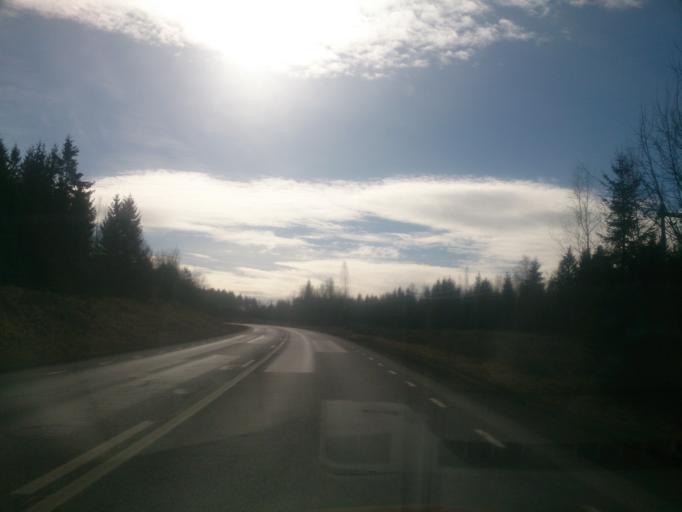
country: SE
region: OEstergoetland
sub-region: Norrkopings Kommun
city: Kimstad
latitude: 58.5344
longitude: 15.9767
